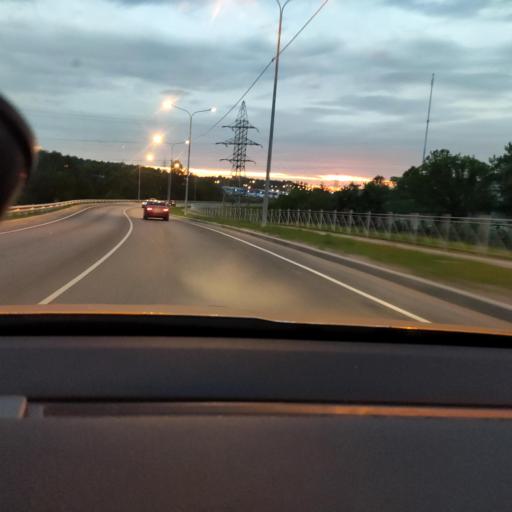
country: RU
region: Moskovskaya
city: Vidnoye
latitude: 55.5346
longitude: 37.7062
